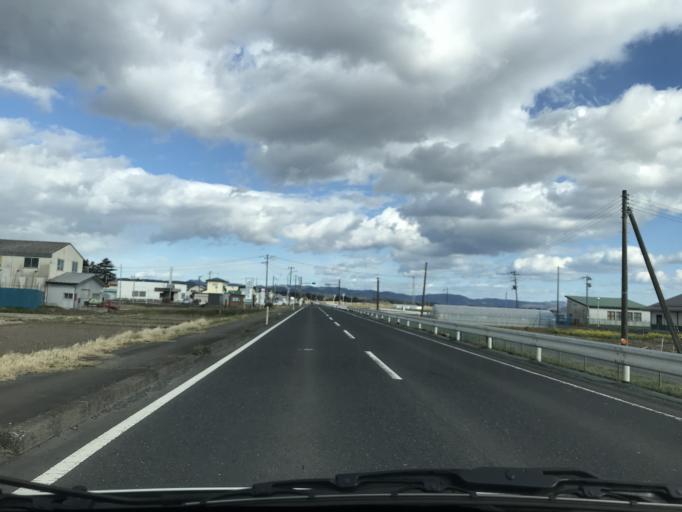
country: JP
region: Miyagi
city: Wakuya
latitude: 38.6274
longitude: 141.1969
